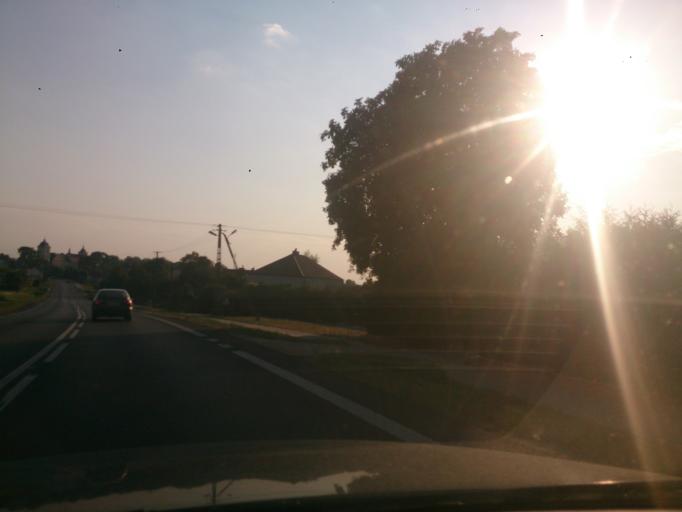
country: PL
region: Subcarpathian Voivodeship
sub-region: Powiat kolbuszowski
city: Majdan Krolewski
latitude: 50.3835
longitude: 21.7506
